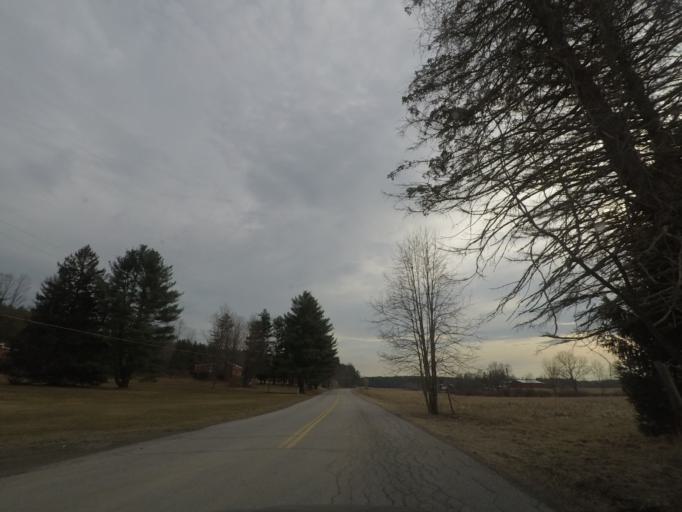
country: US
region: New York
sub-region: Rensselaer County
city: Hoosick Falls
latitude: 42.8767
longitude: -73.4463
